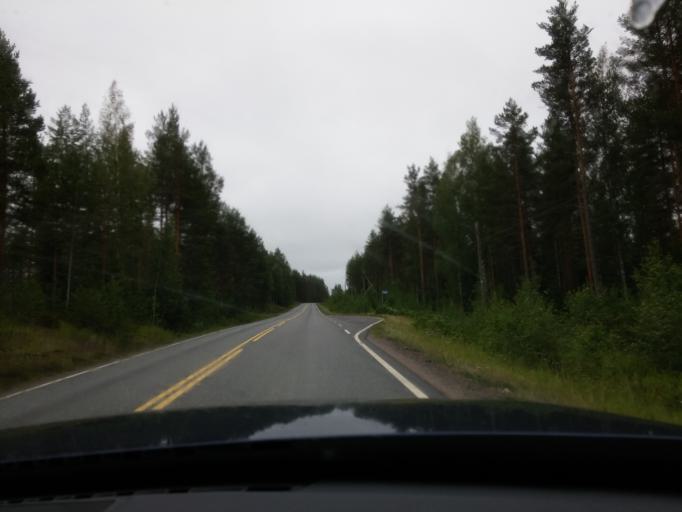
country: FI
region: Central Finland
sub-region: Joutsa
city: Joutsa
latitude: 61.7925
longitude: 26.0110
